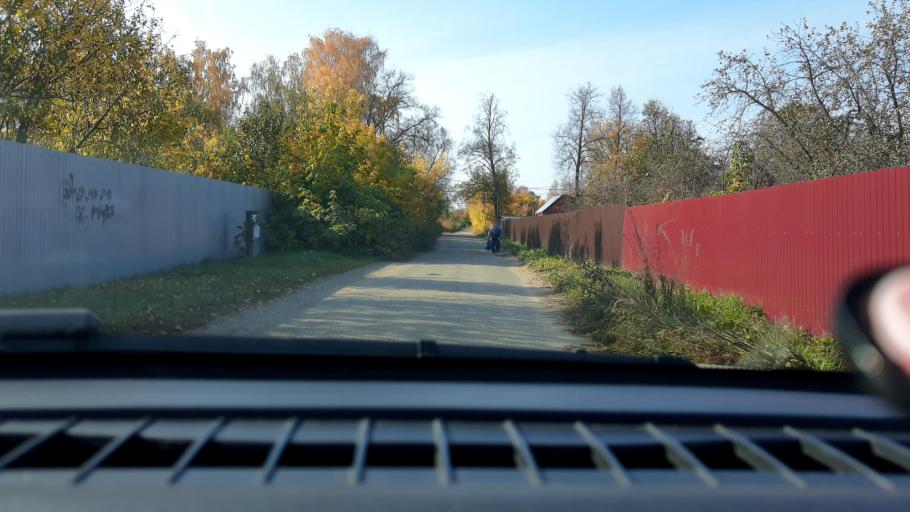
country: RU
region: Nizjnij Novgorod
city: Gorbatovka
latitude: 56.2131
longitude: 43.7577
